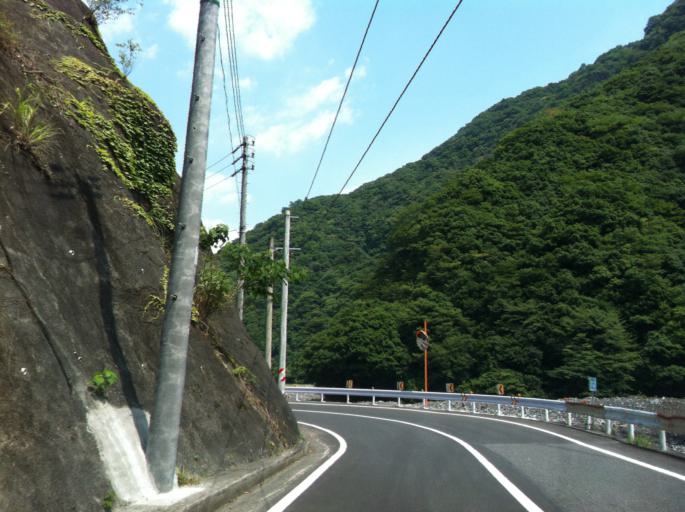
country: JP
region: Shizuoka
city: Shizuoka-shi
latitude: 35.2143
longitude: 138.3514
